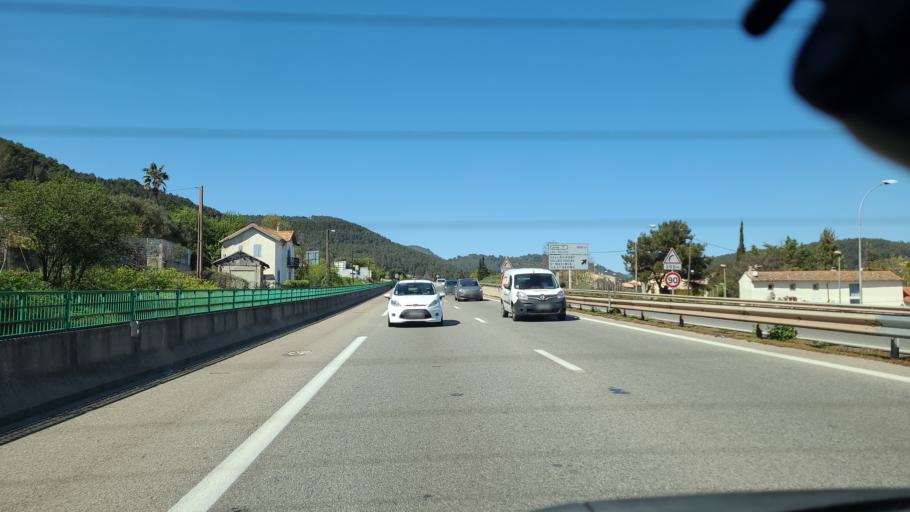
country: FR
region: Provence-Alpes-Cote d'Azur
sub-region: Departement du Var
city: Sollies-Ville
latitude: 43.1855
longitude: 6.0411
